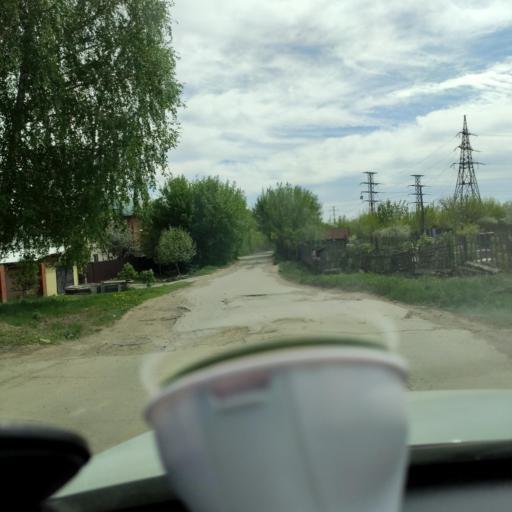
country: RU
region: Samara
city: Petra-Dubrava
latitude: 53.2971
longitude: 50.3042
